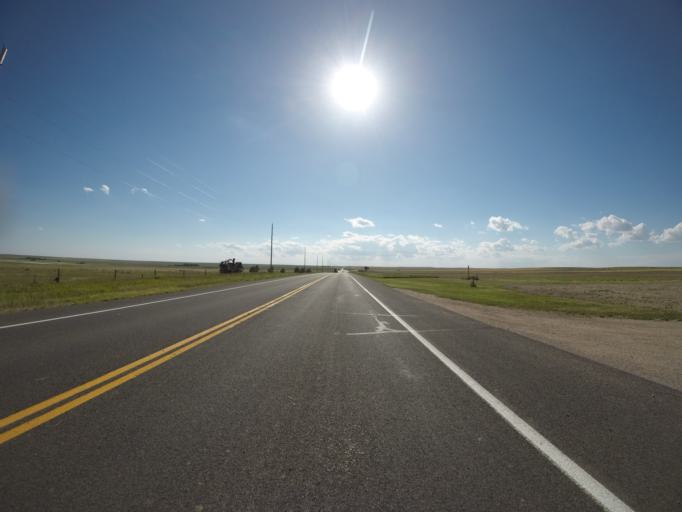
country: US
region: Colorado
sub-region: Morgan County
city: Brush
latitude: 40.6100
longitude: -103.6680
